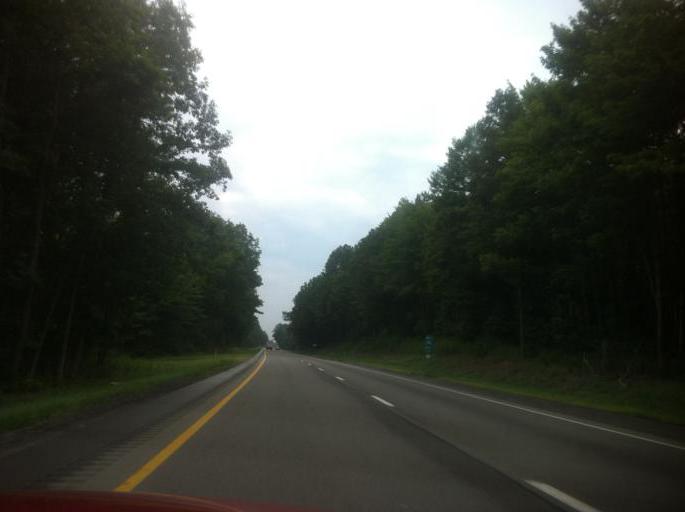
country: US
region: Pennsylvania
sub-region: Jefferson County
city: Brookville
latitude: 41.1797
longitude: -79.1279
